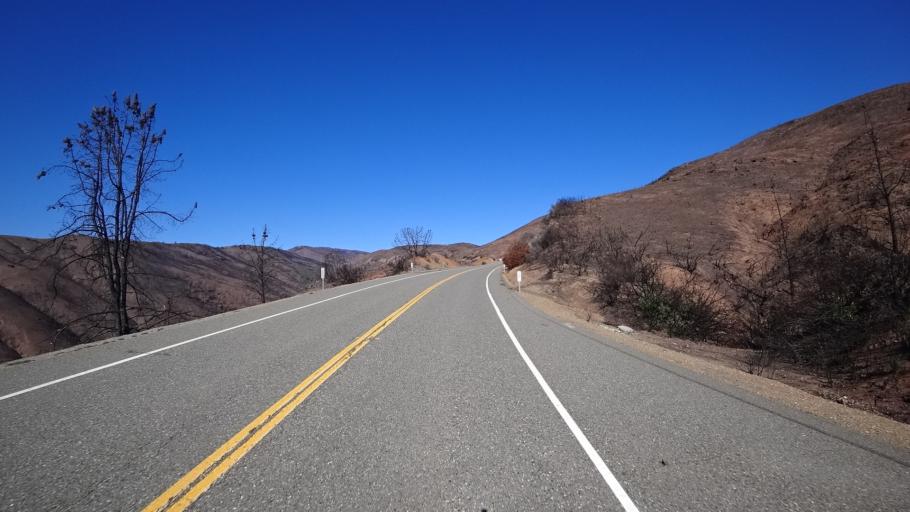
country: US
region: California
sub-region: Tehama County
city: Rancho Tehama Reserve
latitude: 39.6583
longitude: -122.6266
